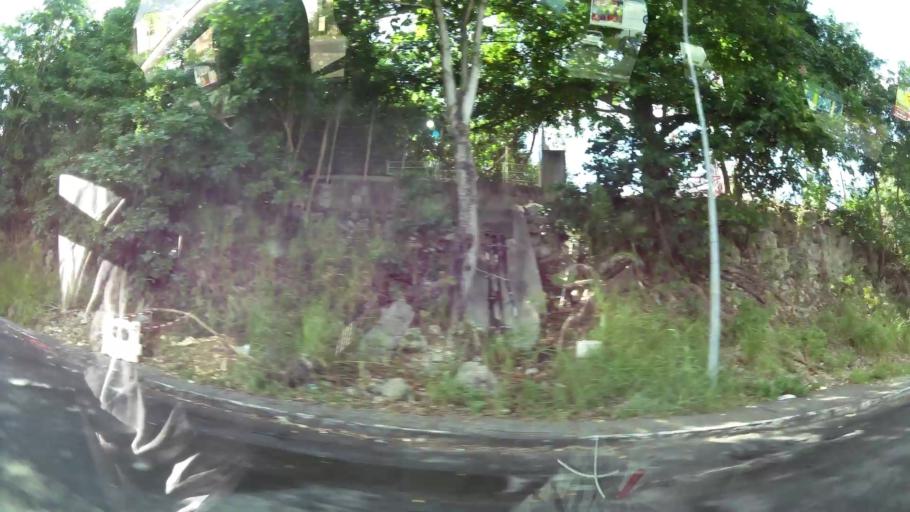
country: GP
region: Guadeloupe
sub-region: Guadeloupe
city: Pointe-a-Pitre
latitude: 16.2495
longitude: -61.5368
